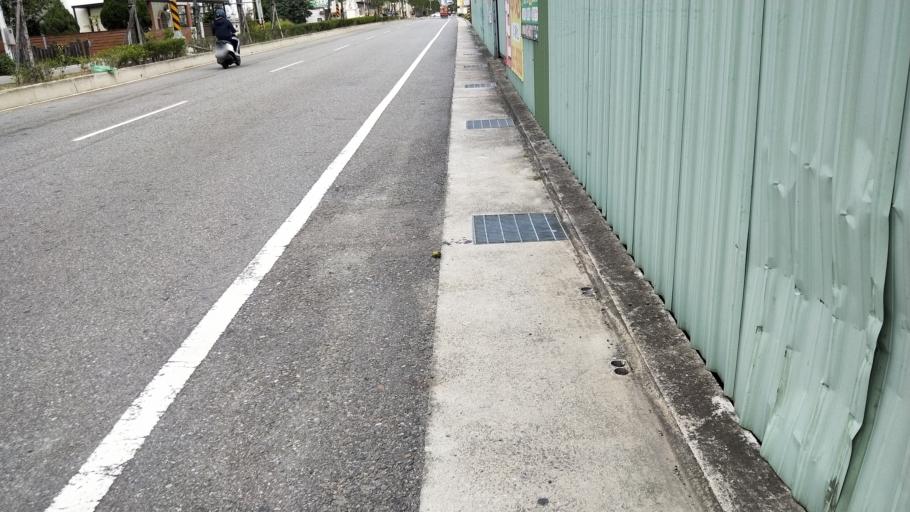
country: TW
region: Taiwan
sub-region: Hsinchu
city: Hsinchu
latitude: 24.6888
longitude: 120.8948
